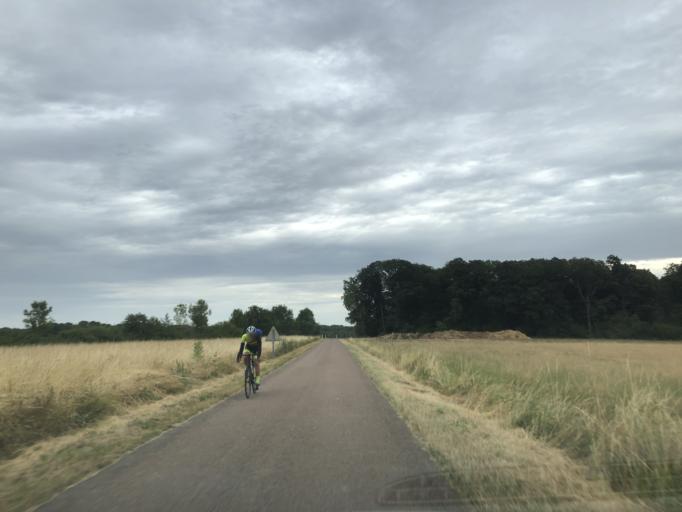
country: FR
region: Bourgogne
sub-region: Departement de l'Yonne
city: Aillant-sur-Tholon
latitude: 47.9010
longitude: 3.3017
